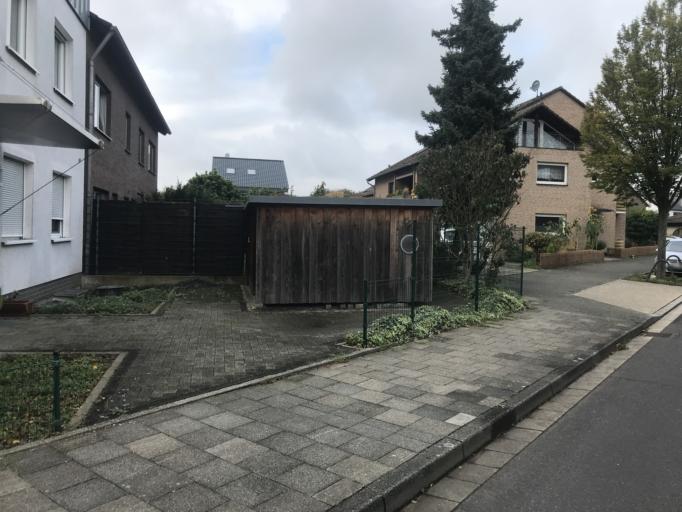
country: DE
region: North Rhine-Westphalia
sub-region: Regierungsbezirk Dusseldorf
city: Neuss
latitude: 51.1244
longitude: 6.7326
